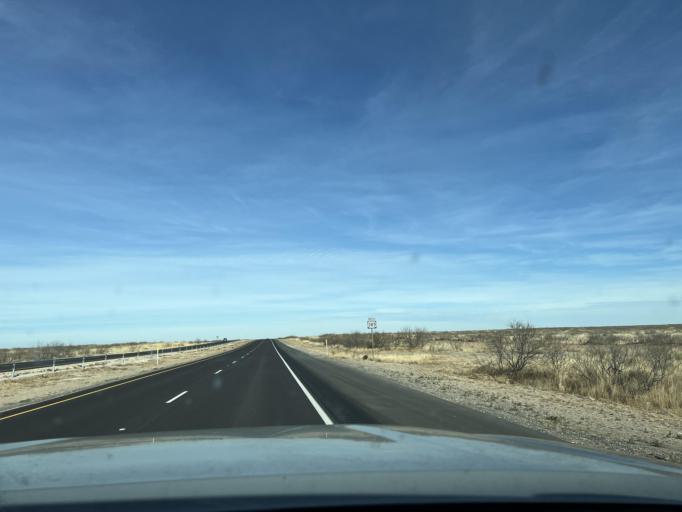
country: US
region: Texas
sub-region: Ector County
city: Gardendale
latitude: 32.0315
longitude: -102.4328
